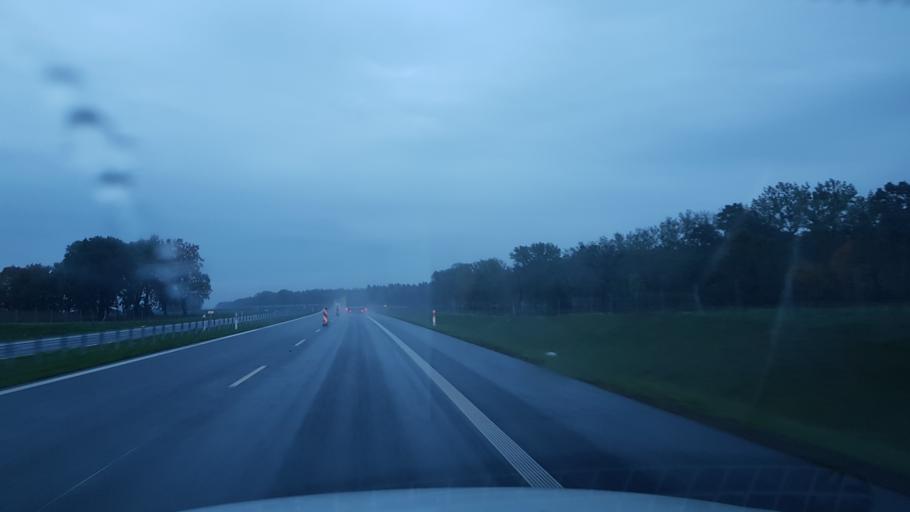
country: PL
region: West Pomeranian Voivodeship
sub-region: Powiat gryficki
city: Ploty
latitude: 53.8303
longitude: 15.2882
